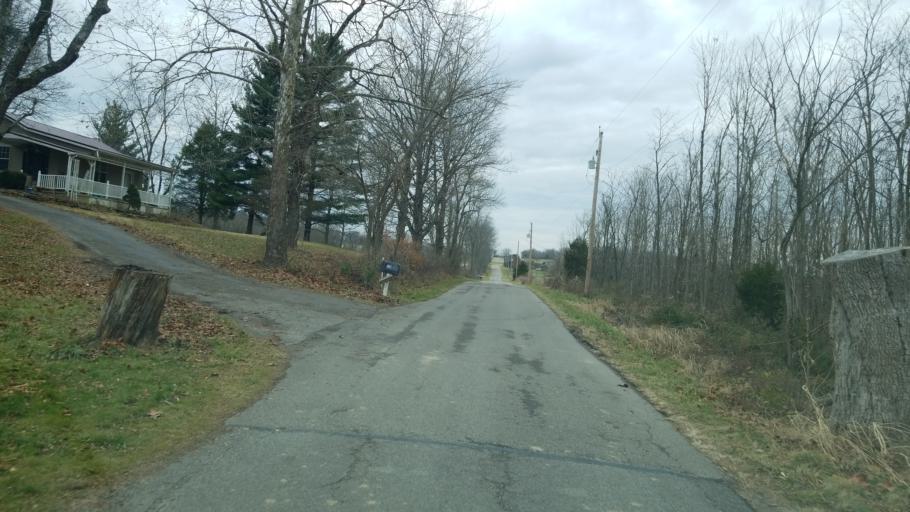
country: US
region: Ohio
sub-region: Highland County
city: Greenfield
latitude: 39.2996
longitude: -83.3511
